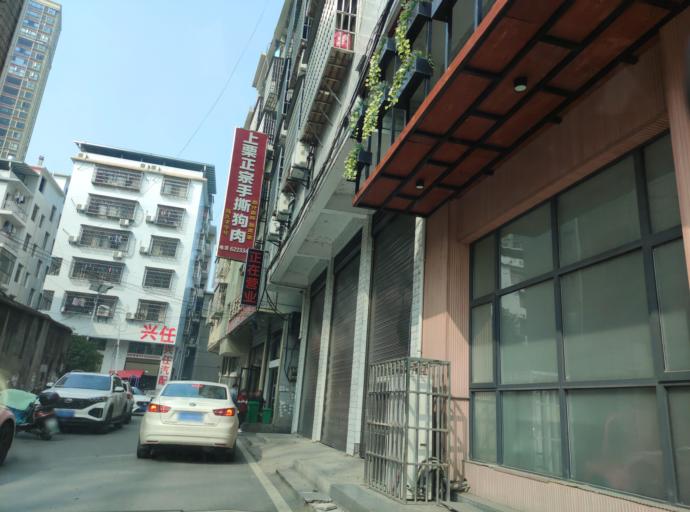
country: CN
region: Jiangxi Sheng
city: Pingxiang
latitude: 27.6456
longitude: 113.8412
